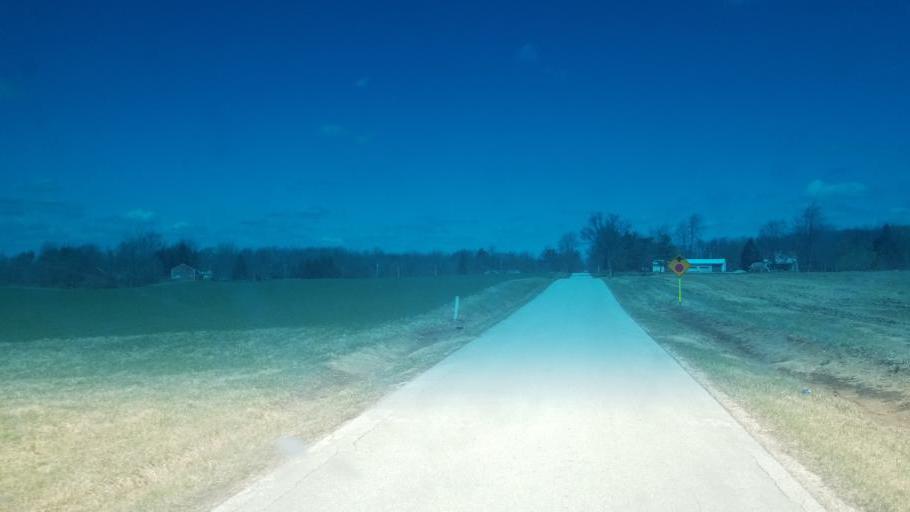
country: US
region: Ohio
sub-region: Crawford County
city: Bucyrus
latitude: 40.8353
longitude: -83.0739
